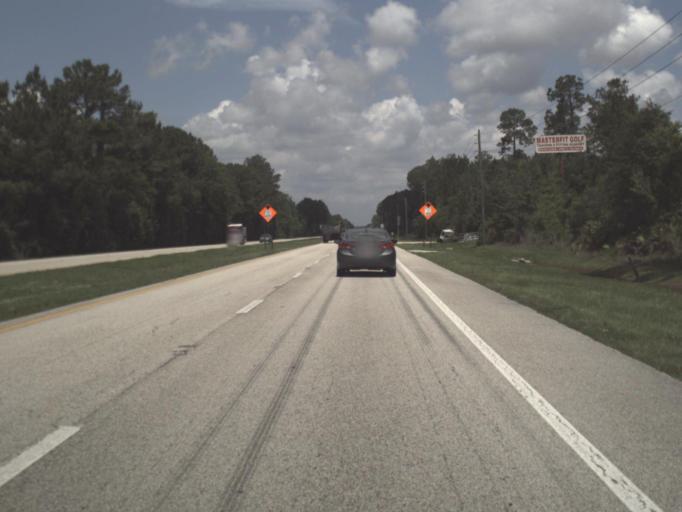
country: US
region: Florida
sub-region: Saint Johns County
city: Palm Valley
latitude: 30.1211
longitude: -81.4954
